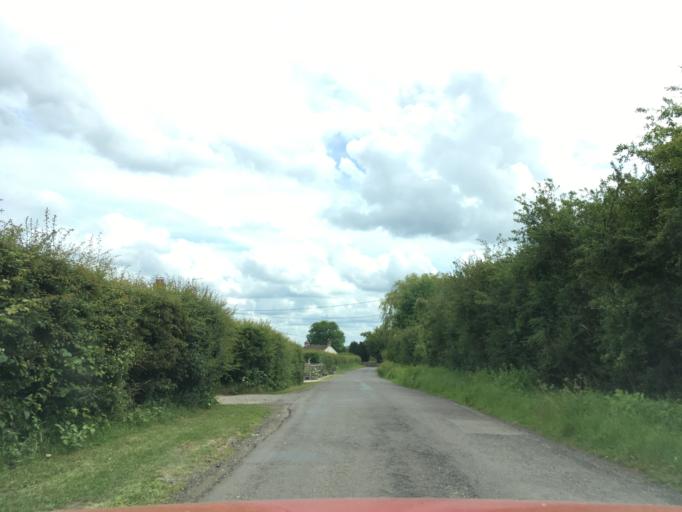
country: GB
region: England
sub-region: Wiltshire
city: Royal Wootton Bassett
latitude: 51.5654
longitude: -1.8916
